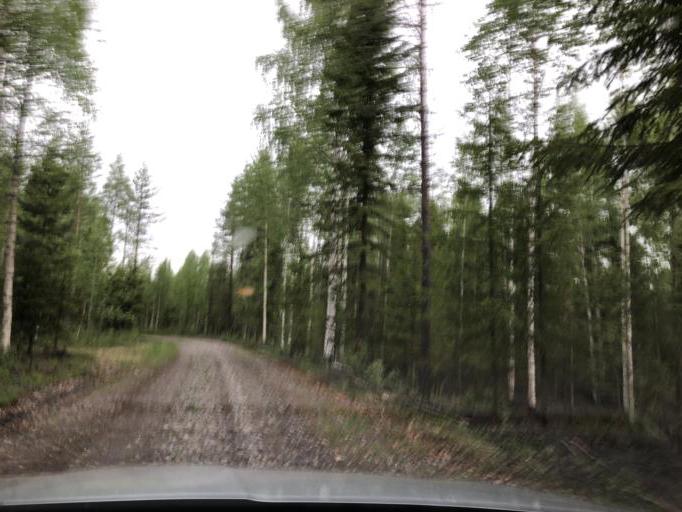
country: SE
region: Norrbotten
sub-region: Pitea Kommun
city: Roknas
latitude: 65.4014
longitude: 21.2624
